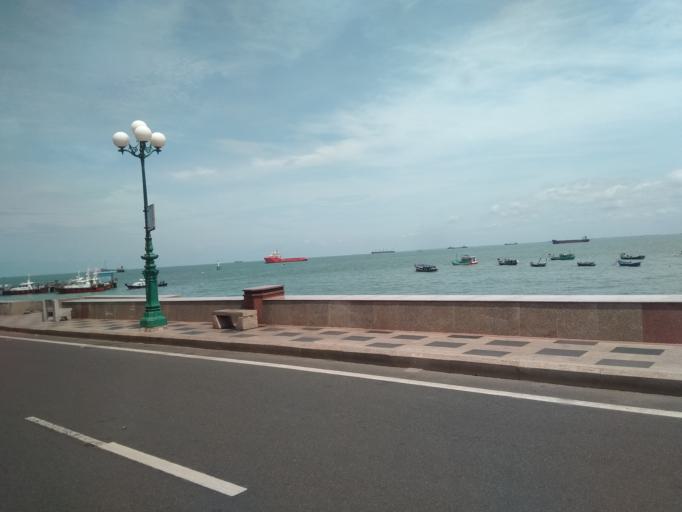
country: VN
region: Ba Ria-Vung Tau
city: Vung Tau
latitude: 10.3407
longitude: 107.0730
